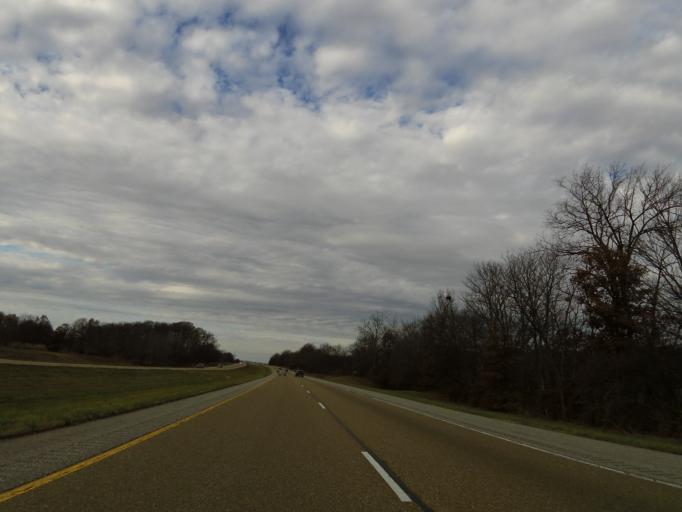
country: US
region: Illinois
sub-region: Clinton County
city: Wamac
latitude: 38.3893
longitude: -89.2029
